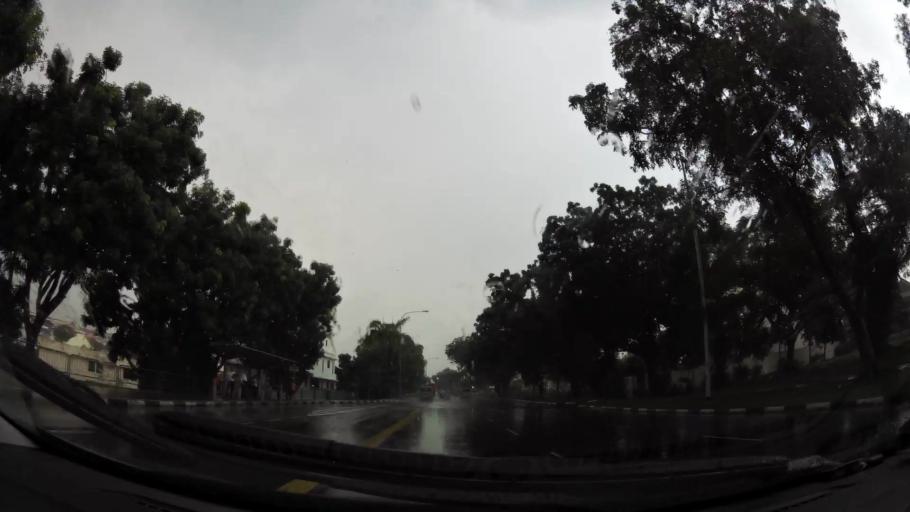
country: SG
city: Singapore
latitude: 1.3213
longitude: 103.9173
